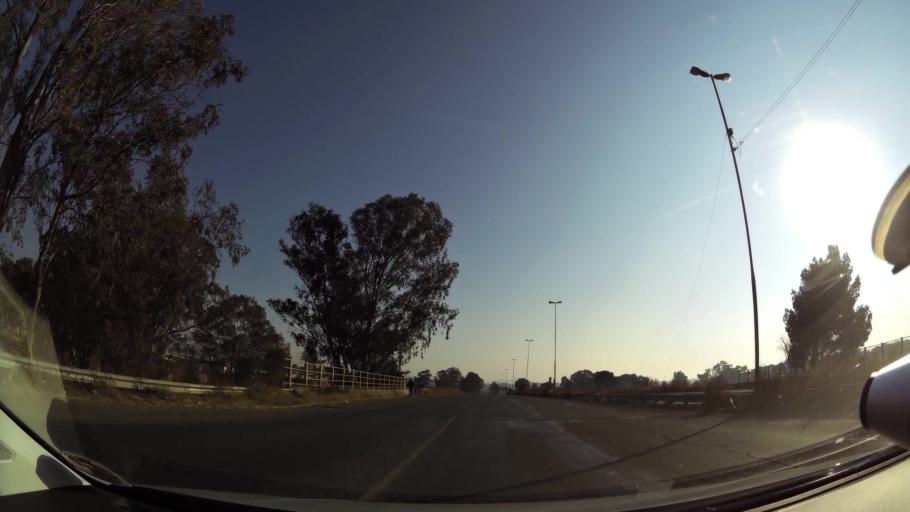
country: ZA
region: Orange Free State
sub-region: Mangaung Metropolitan Municipality
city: Bloemfontein
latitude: -29.1345
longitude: 26.2671
